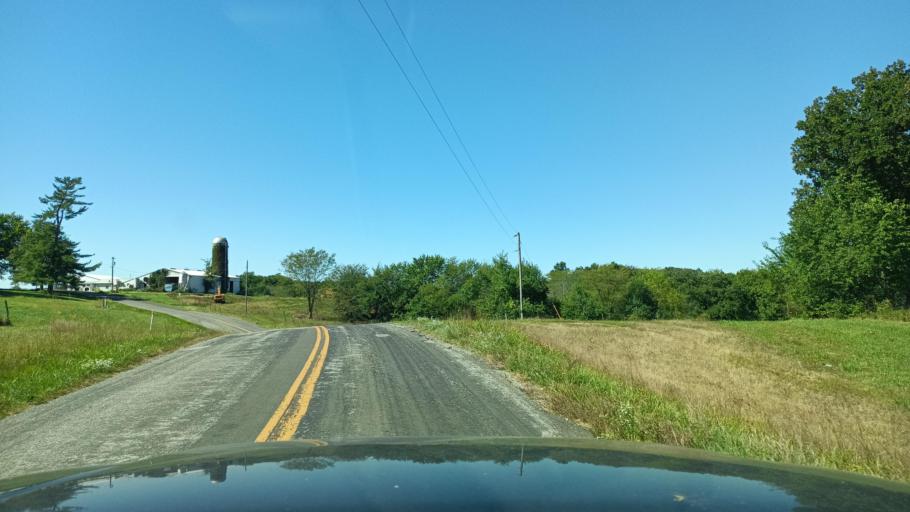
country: US
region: Missouri
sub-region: Scotland County
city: Memphis
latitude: 40.3547
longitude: -92.2352
